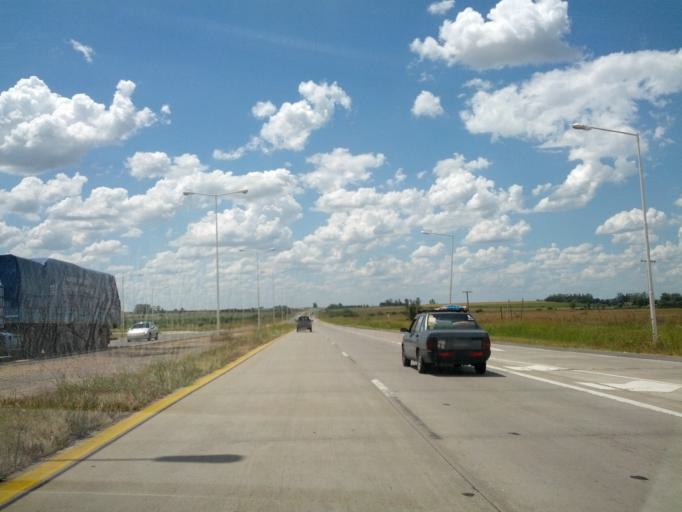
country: AR
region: Entre Rios
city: Gualeguaychu
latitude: -32.8966
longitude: -58.5522
